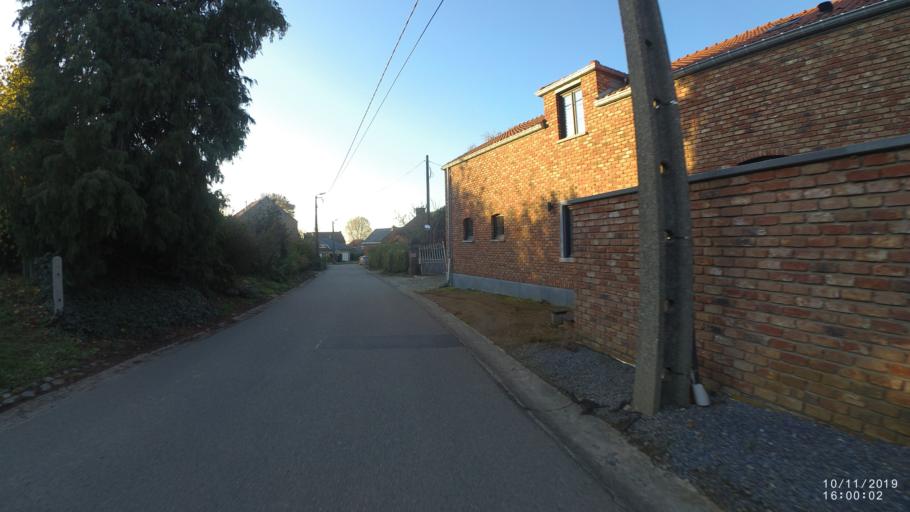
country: BE
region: Flanders
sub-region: Provincie Vlaams-Brabant
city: Lubbeek
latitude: 50.9026
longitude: 4.8797
